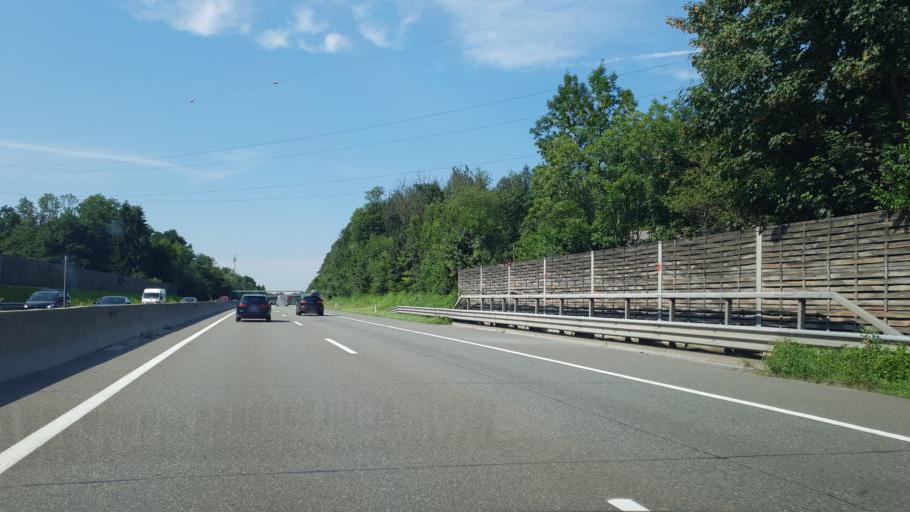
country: AT
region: Salzburg
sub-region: Politischer Bezirk Hallein
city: Puch bei Hallein
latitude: 47.7126
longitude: 13.0986
